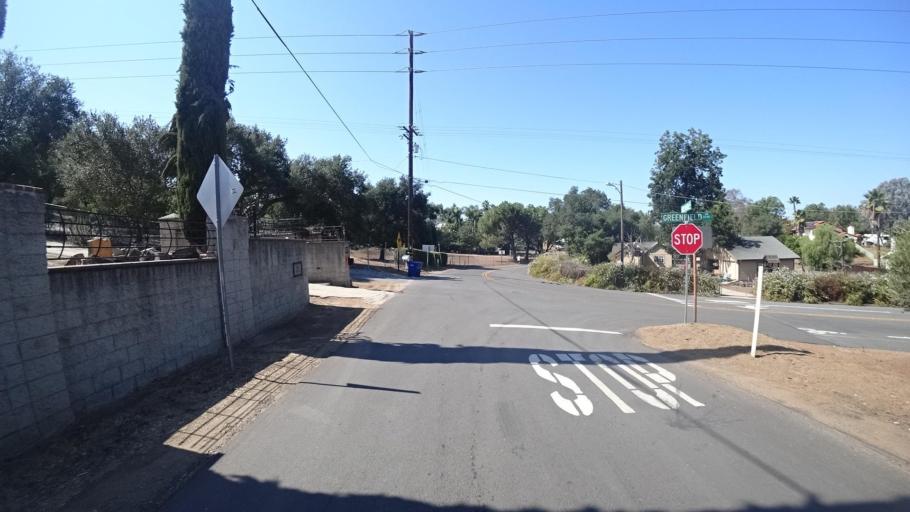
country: US
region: California
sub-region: San Diego County
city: Granite Hills
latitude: 32.7941
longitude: -116.9008
